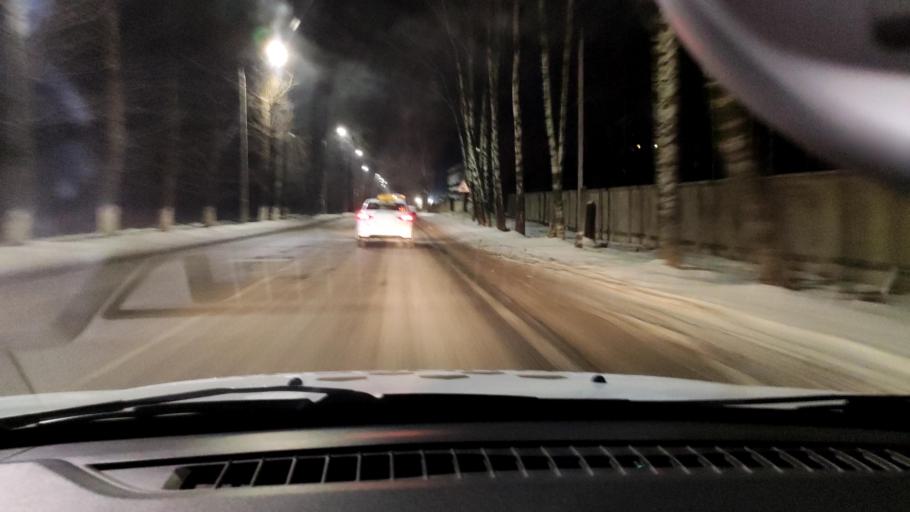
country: RU
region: Perm
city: Kultayevo
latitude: 57.9846
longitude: 55.9213
